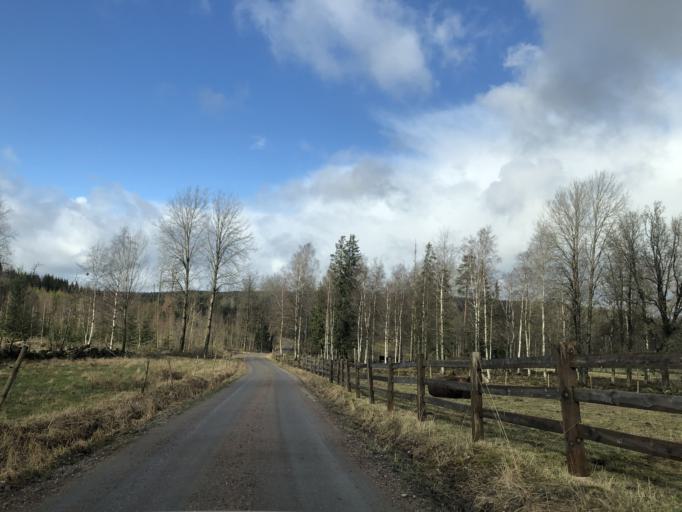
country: SE
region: Vaestra Goetaland
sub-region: Boras Kommun
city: Dalsjofors
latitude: 57.8248
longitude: 13.2063
